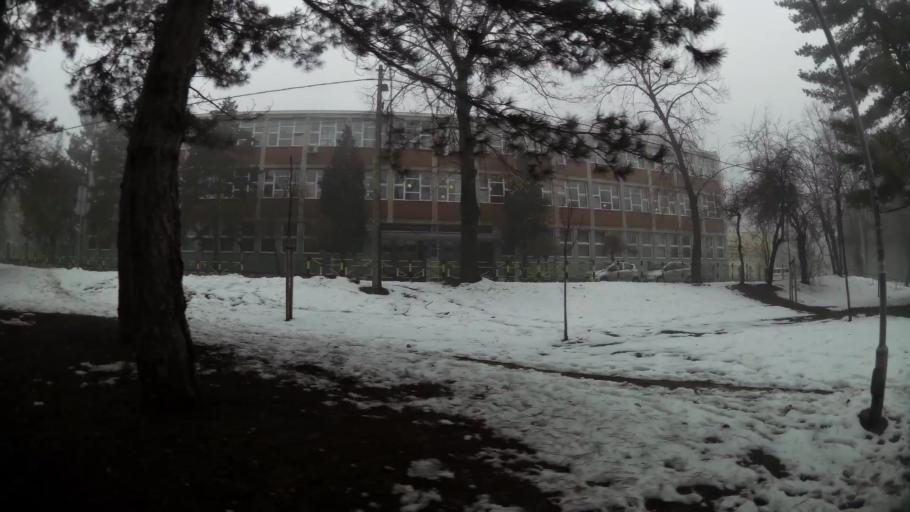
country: RS
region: Central Serbia
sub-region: Belgrade
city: Vozdovac
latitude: 44.7752
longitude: 20.4659
